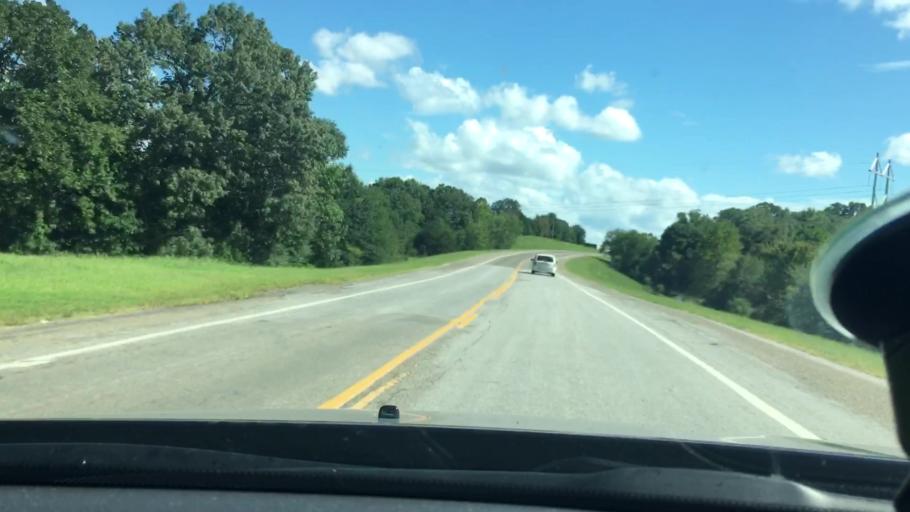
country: US
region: Oklahoma
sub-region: Sequoyah County
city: Vian
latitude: 35.5169
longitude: -94.9718
